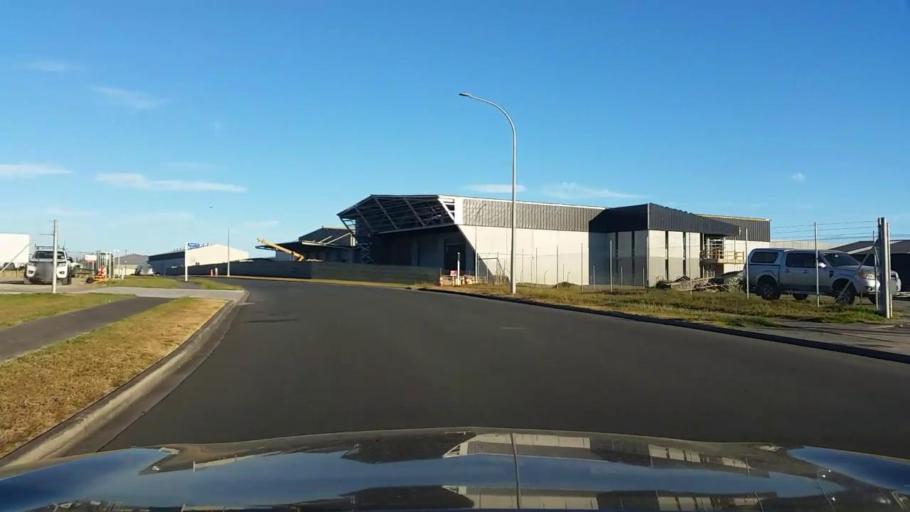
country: NZ
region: Waikato
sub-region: Matamata-Piako District
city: Matamata
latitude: -37.8172
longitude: 175.7964
